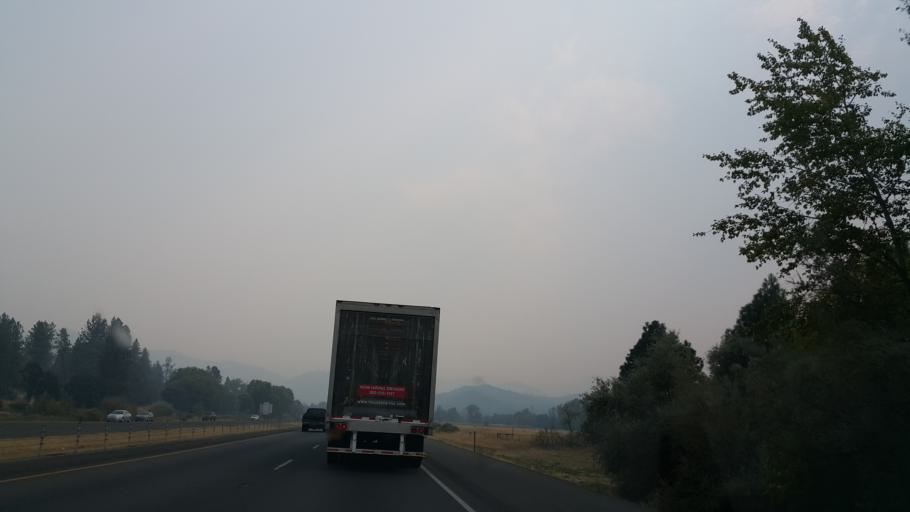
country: US
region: Oregon
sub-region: Jackson County
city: Rogue River
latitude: 42.4197
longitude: -123.1599
